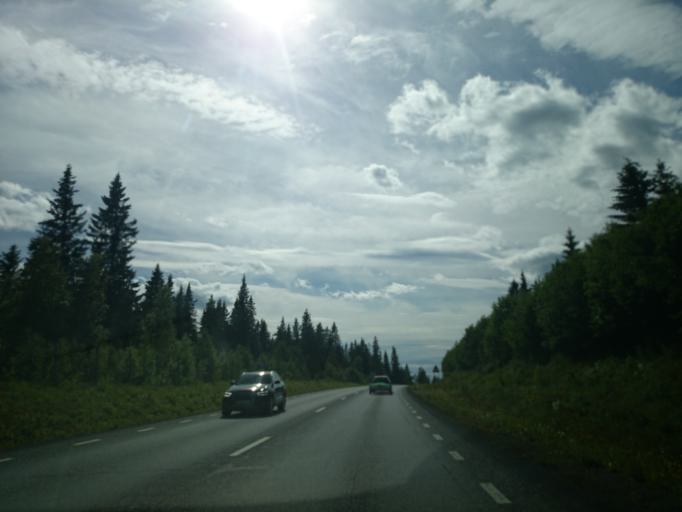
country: SE
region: Jaemtland
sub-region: Krokoms Kommun
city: Valla
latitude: 63.3056
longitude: 13.9101
